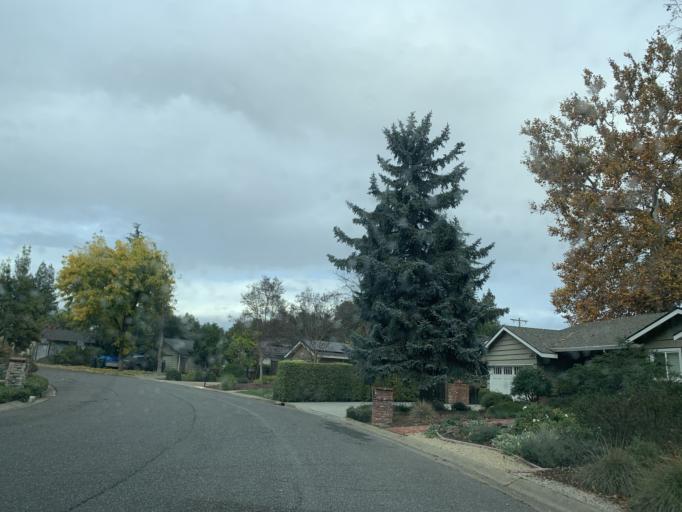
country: US
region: California
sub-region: Santa Clara County
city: Monte Sereno
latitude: 37.2661
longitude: -121.9916
